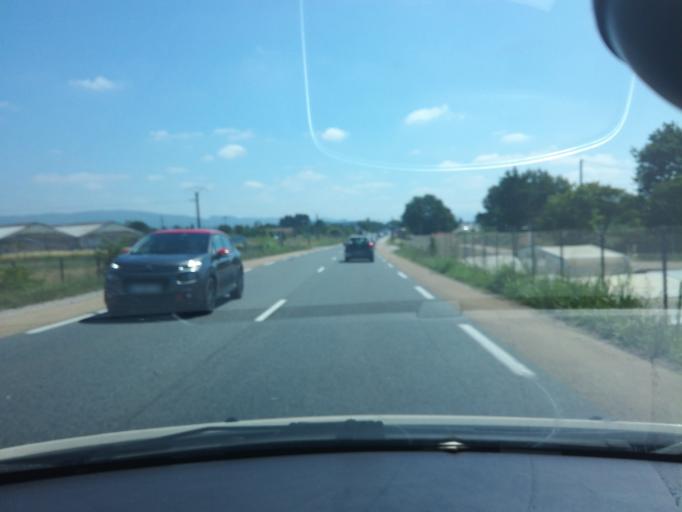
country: FR
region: Provence-Alpes-Cote d'Azur
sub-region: Departement du Var
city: La Motte
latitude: 43.4657
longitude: 6.5396
